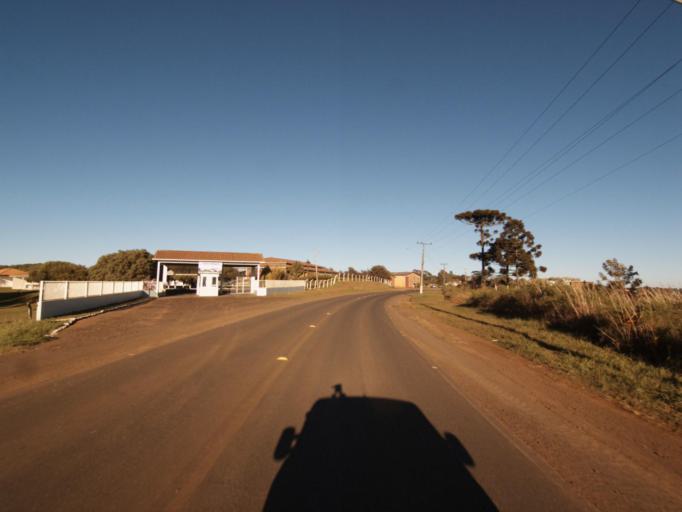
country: AR
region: Misiones
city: Bernardo de Irigoyen
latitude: -26.2694
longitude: -53.6297
